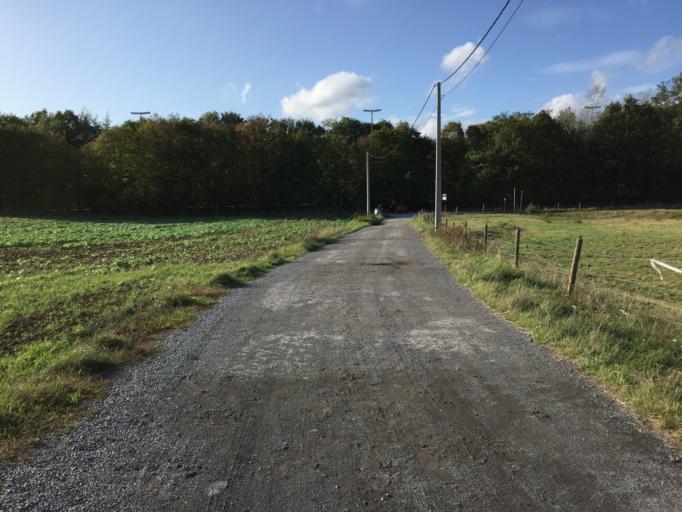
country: BE
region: Wallonia
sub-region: Province du Brabant Wallon
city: Braine-l'Alleud
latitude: 50.6713
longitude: 4.3930
